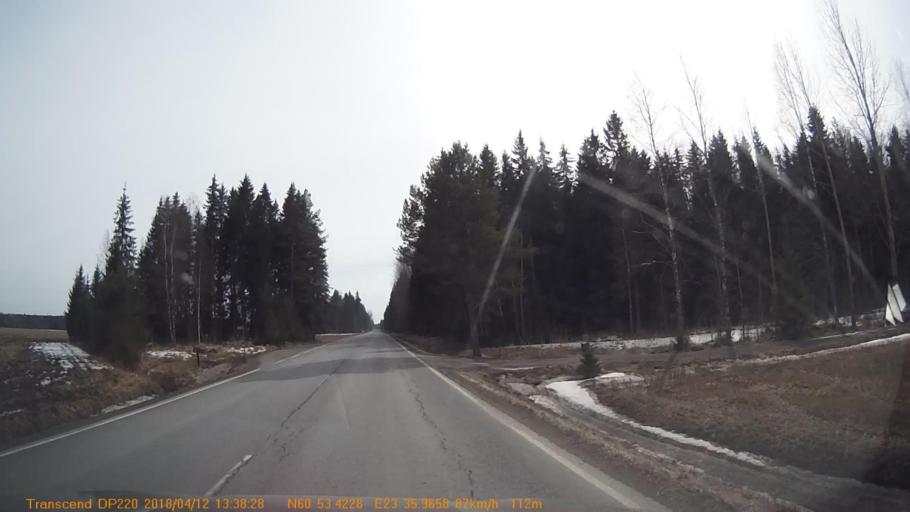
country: FI
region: Haeme
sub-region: Forssa
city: Forssa
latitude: 60.8901
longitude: 23.5996
